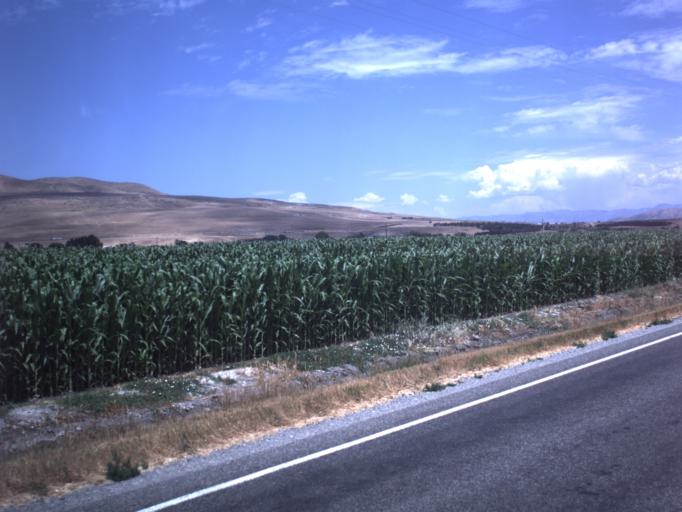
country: US
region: Utah
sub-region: Box Elder County
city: Tremonton
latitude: 41.7096
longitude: -112.2630
